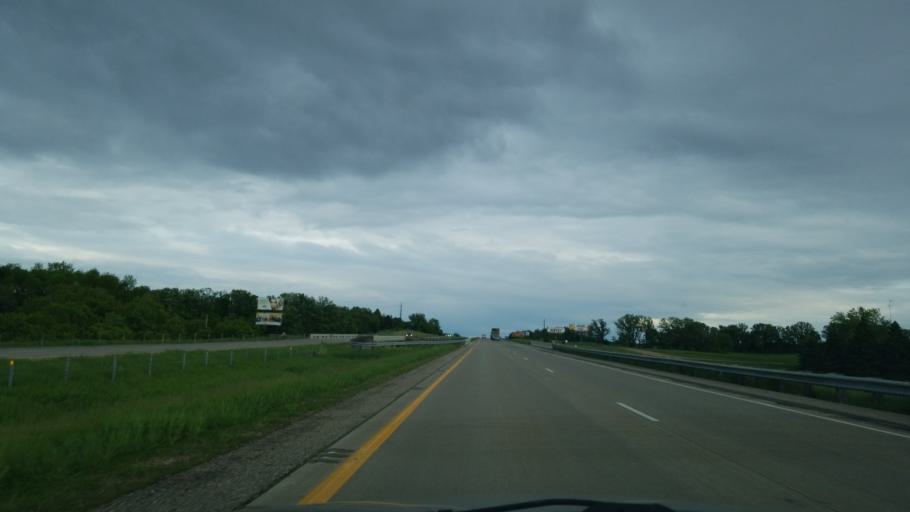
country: US
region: Minnesota
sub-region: Stearns County
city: Sauk Centre
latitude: 45.7390
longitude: -94.9797
